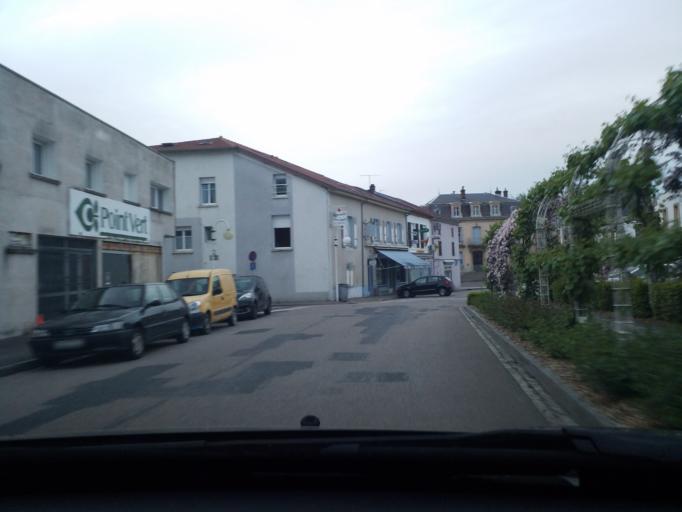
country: FR
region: Lorraine
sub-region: Departement des Vosges
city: Vittel
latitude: 48.1995
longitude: 5.9493
